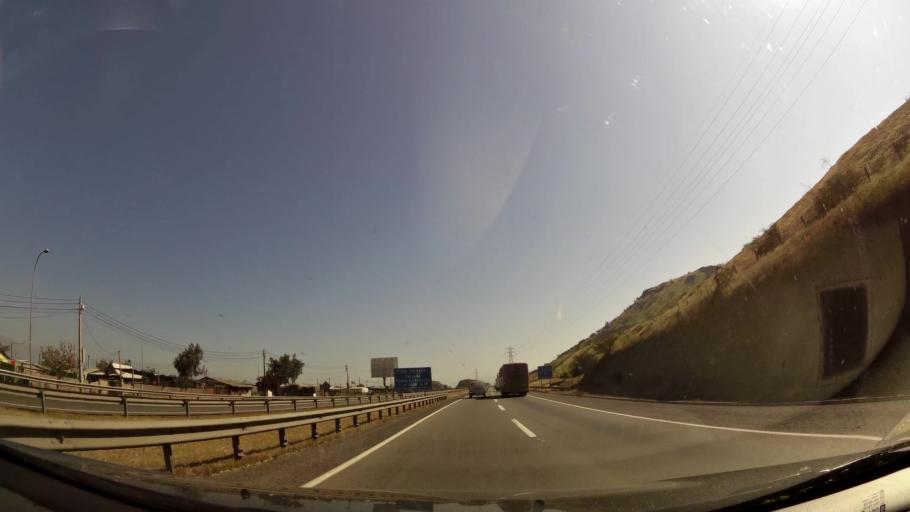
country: CL
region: Santiago Metropolitan
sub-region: Provincia de Chacabuco
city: Chicureo Abajo
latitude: -33.3239
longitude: -70.7054
